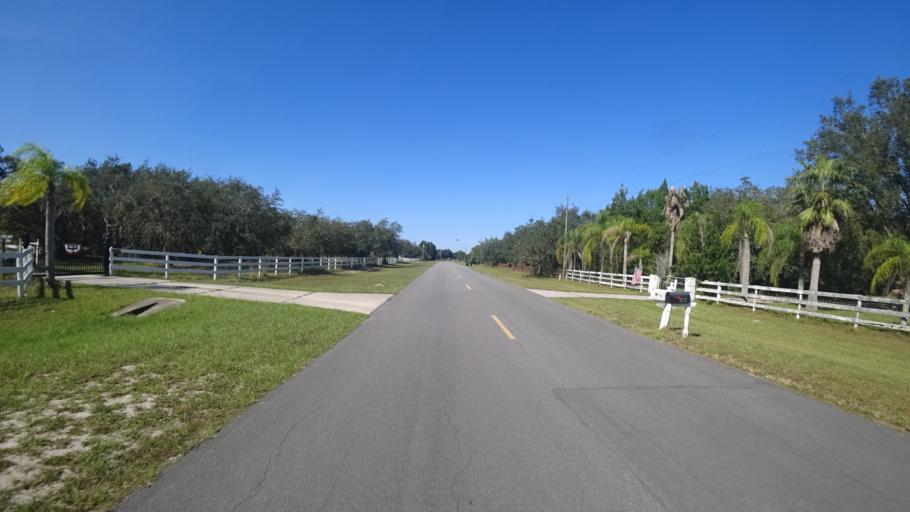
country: US
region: Florida
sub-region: Sarasota County
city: Lake Sarasota
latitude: 27.3591
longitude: -82.2410
